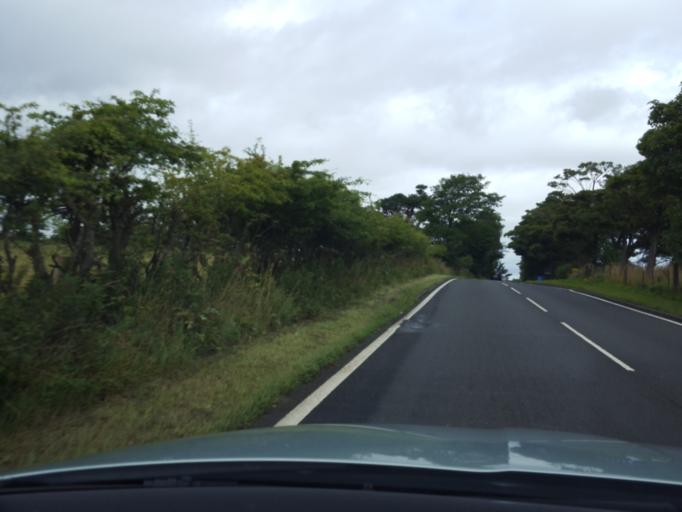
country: GB
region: Scotland
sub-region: Falkirk
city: Polmont
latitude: 55.9522
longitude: -3.6845
